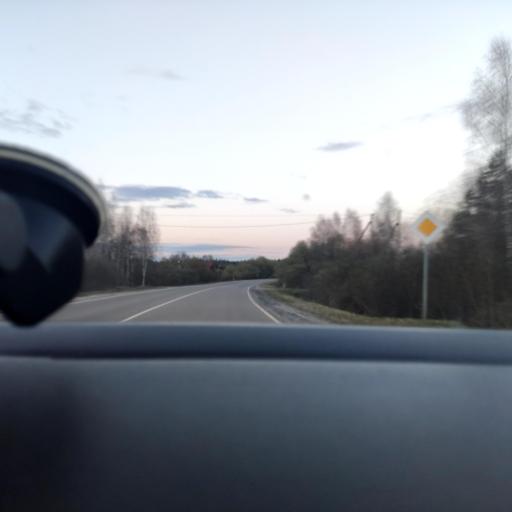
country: RU
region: Moskovskaya
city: Shaturtorf
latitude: 55.4560
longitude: 39.4560
